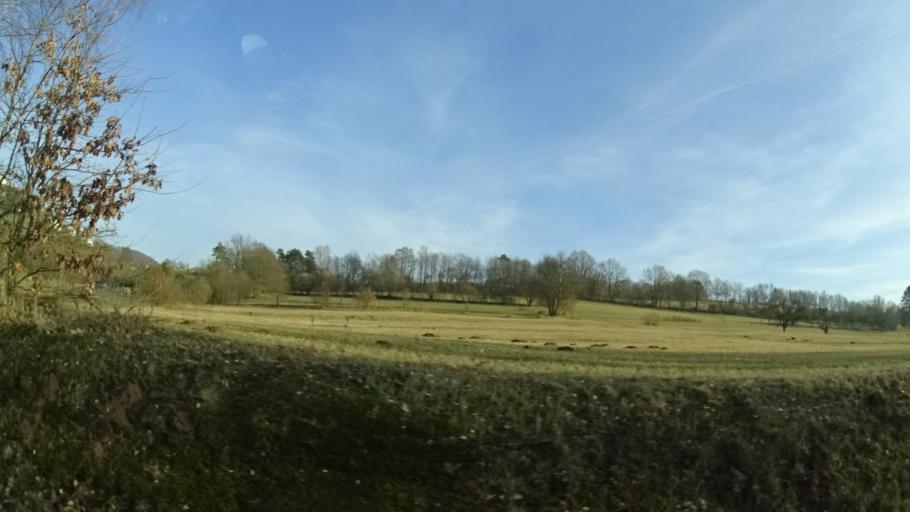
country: DE
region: Bavaria
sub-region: Regierungsbezirk Unterfranken
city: Zeitlofs
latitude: 50.2989
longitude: 9.6611
